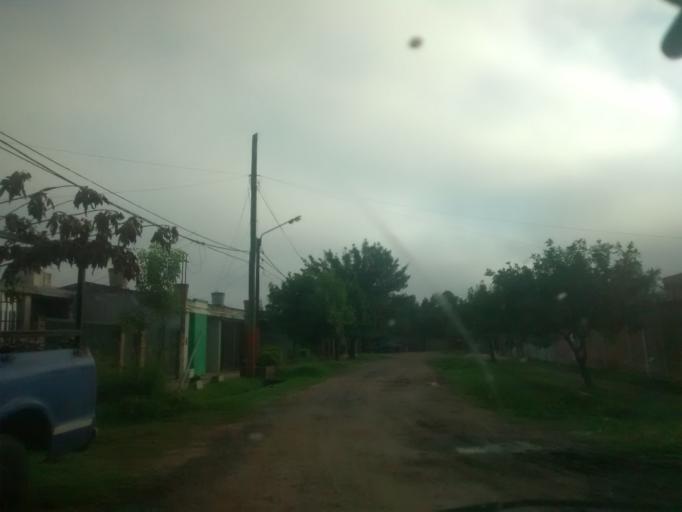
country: AR
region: Chaco
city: Resistencia
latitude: -27.4702
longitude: -58.9892
